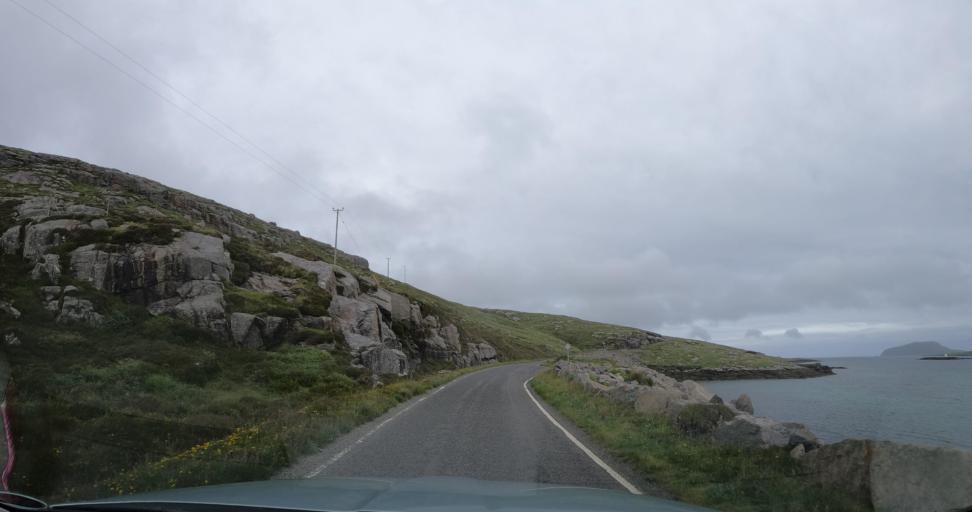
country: GB
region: Scotland
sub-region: Eilean Siar
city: Barra
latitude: 56.9482
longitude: -7.5232
